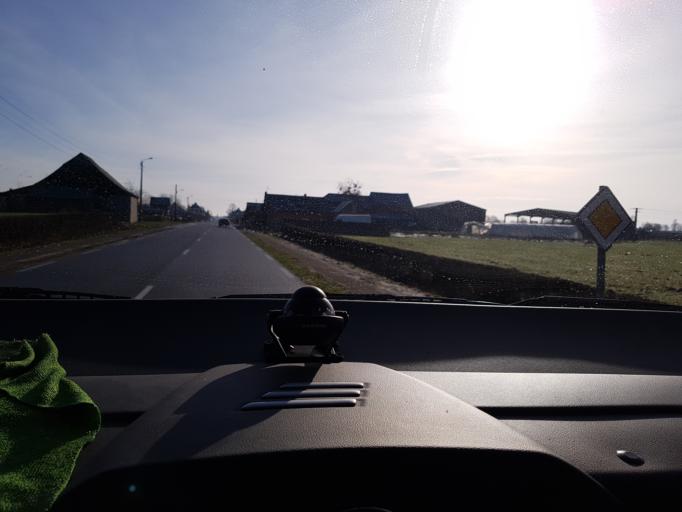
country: FR
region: Nord-Pas-de-Calais
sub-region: Departement du Nord
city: Sains-du-Nord
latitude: 50.0939
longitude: 3.9887
